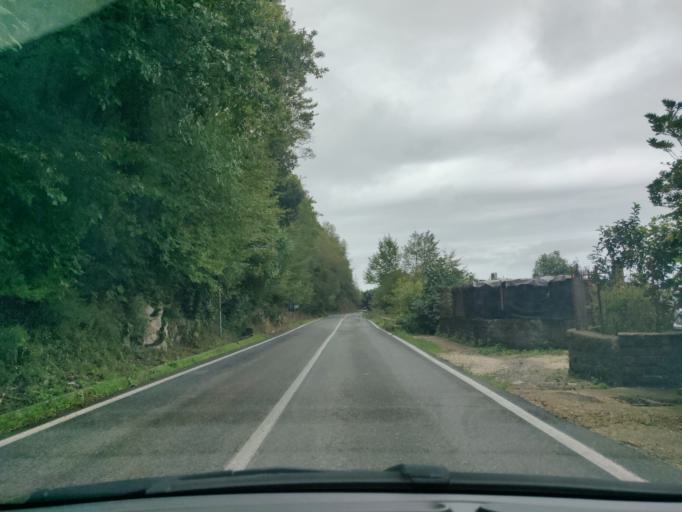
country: IT
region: Latium
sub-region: Citta metropolitana di Roma Capitale
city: Allumiere
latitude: 42.1531
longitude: 11.9004
